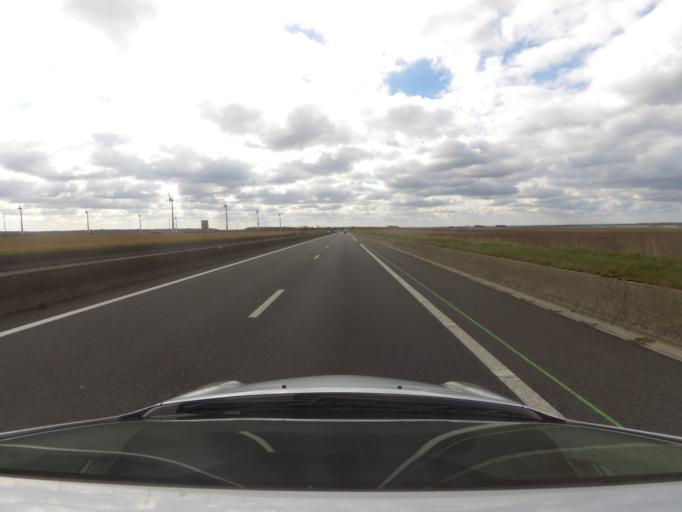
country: FR
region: Picardie
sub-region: Departement de la Somme
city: Rue
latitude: 50.3134
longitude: 1.7224
